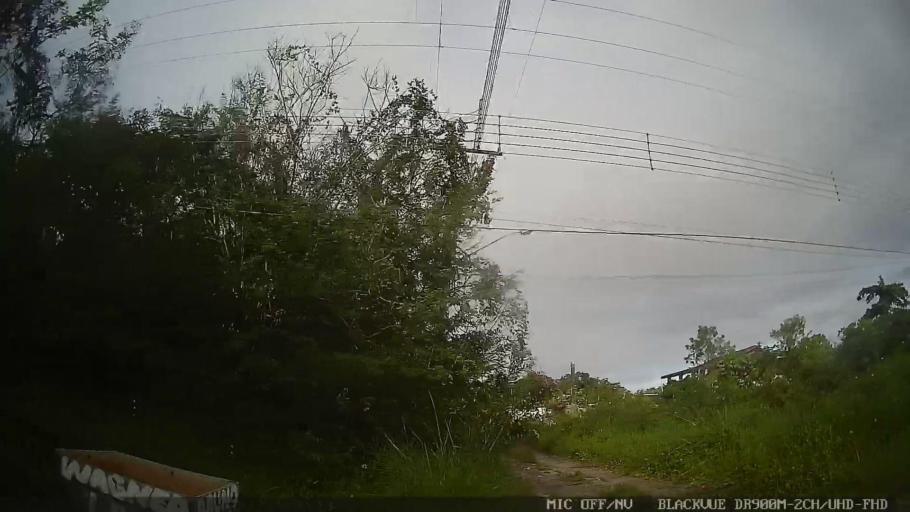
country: BR
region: Sao Paulo
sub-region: Peruibe
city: Peruibe
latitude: -24.2368
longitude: -46.9144
